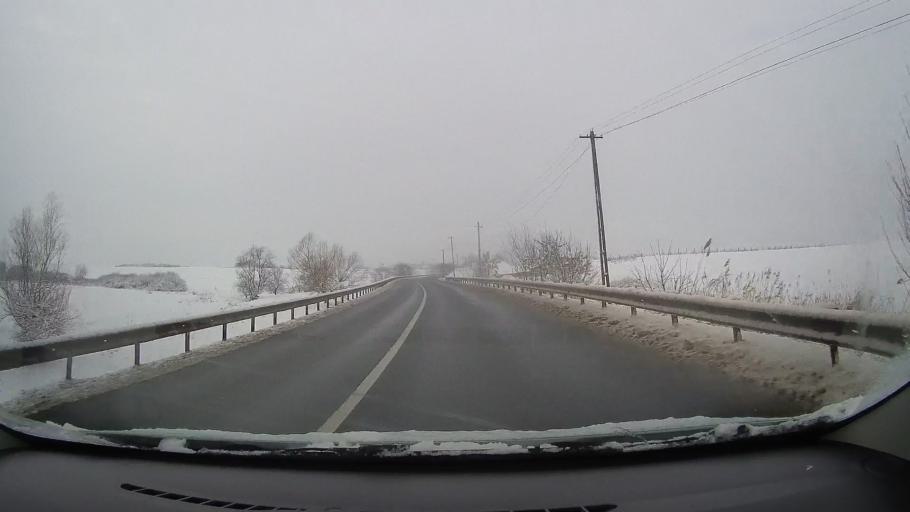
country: RO
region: Alba
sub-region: Municipiul Sebes
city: Lancram
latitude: 45.9832
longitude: 23.5157
